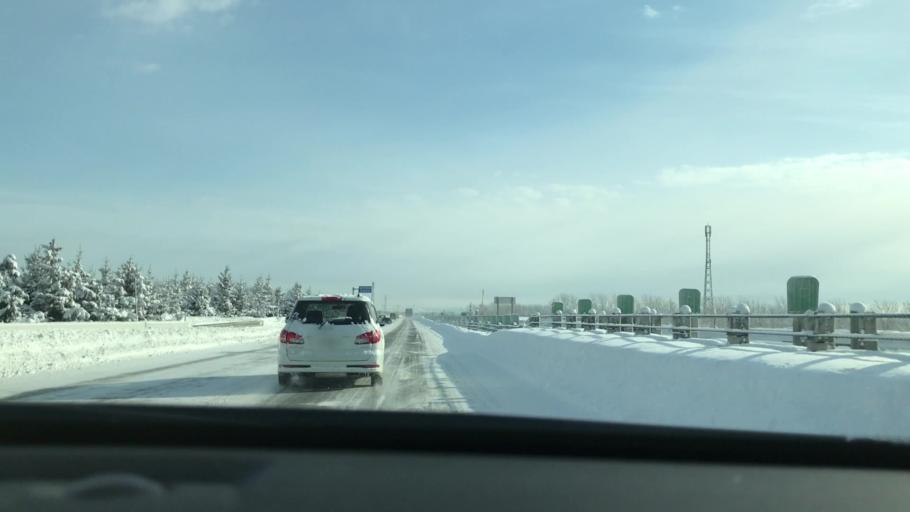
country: JP
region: Hokkaido
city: Ebetsu
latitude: 43.0866
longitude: 141.4493
